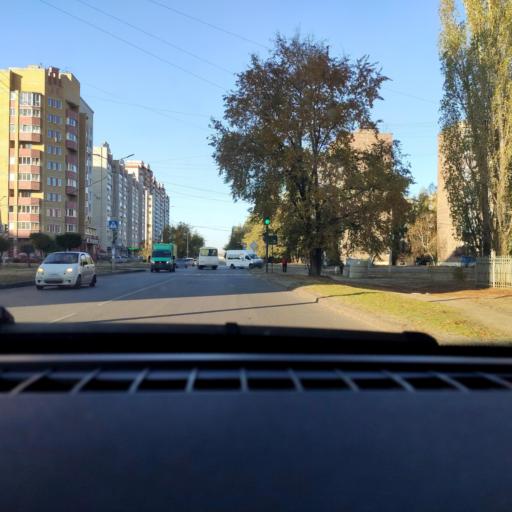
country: RU
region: Voronezj
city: Maslovka
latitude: 51.5949
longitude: 39.2448
